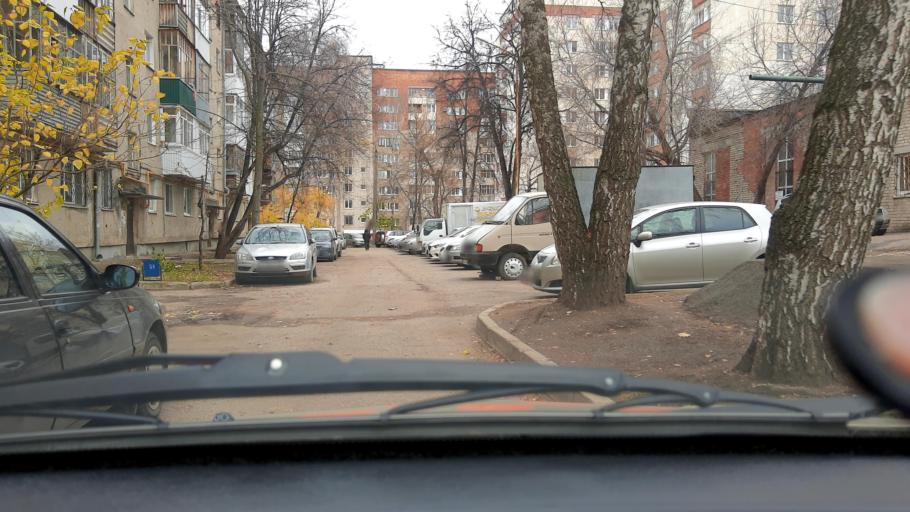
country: RU
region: Bashkortostan
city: Ufa
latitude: 54.7337
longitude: 55.9732
